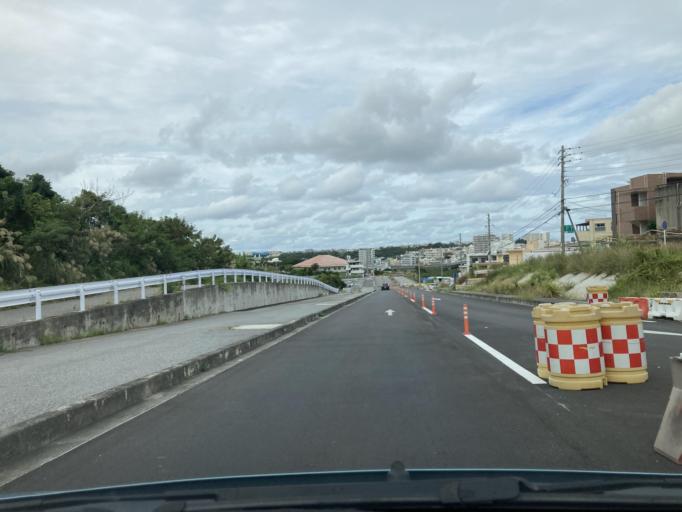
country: JP
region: Okinawa
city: Tomigusuku
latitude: 26.1705
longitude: 127.6768
